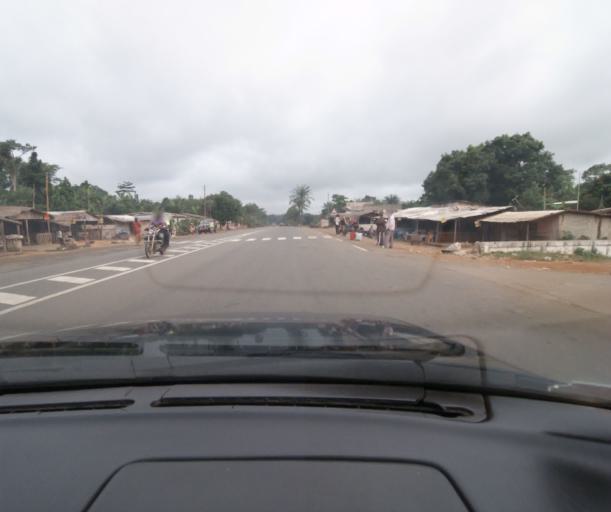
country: CM
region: Centre
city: Obala
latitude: 4.1636
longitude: 11.5015
